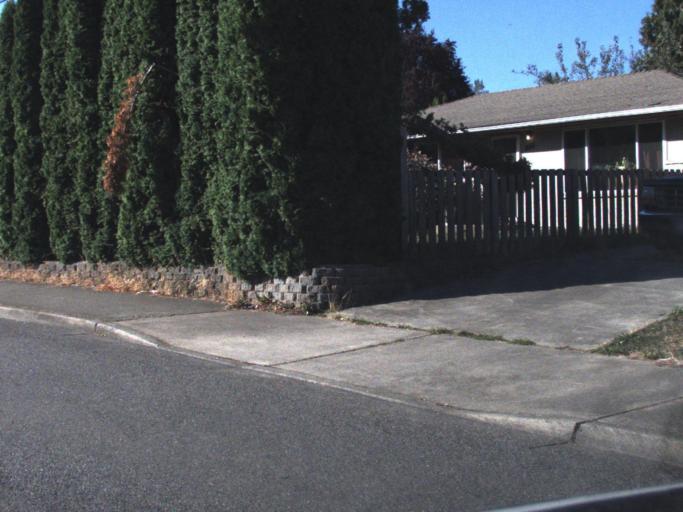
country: US
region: Washington
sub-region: King County
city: East Hill-Meridian
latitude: 47.4118
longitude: -122.1971
